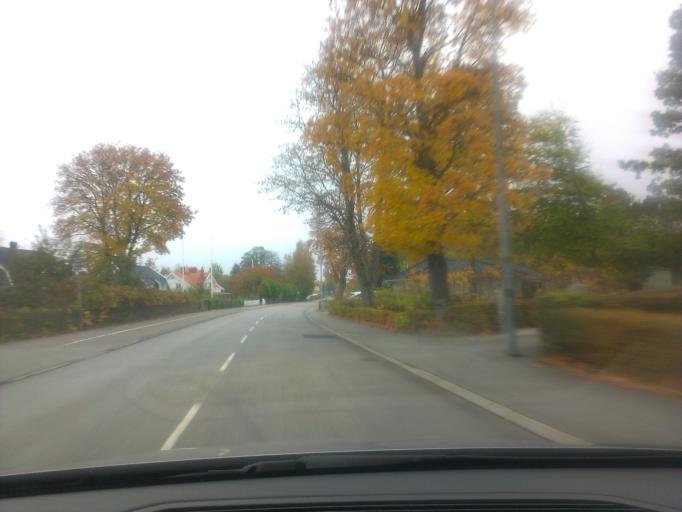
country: SE
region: Kronoberg
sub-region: Vaxjo Kommun
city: Vaexjoe
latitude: 56.9035
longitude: 14.7389
